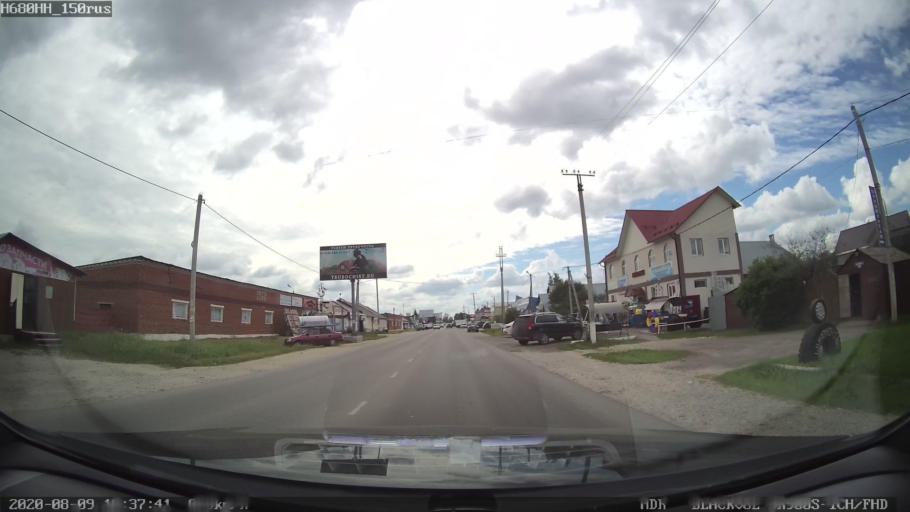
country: RU
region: Tula
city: Zaokskiy
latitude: 54.7373
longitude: 37.3968
